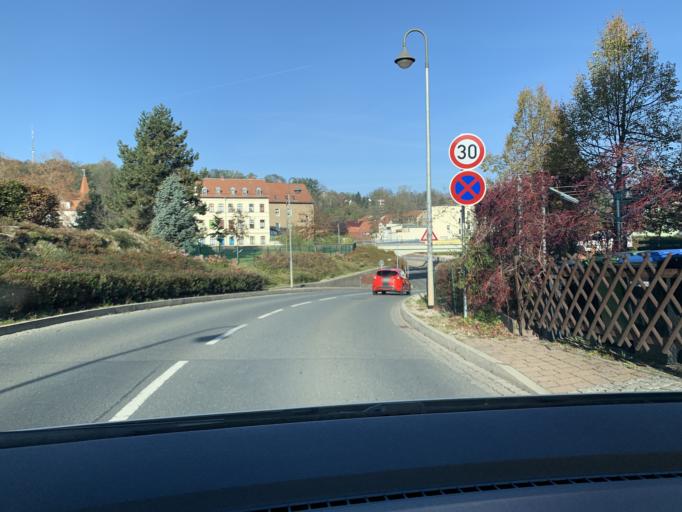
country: DE
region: Thuringia
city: Schmolln
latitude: 50.8942
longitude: 12.3499
